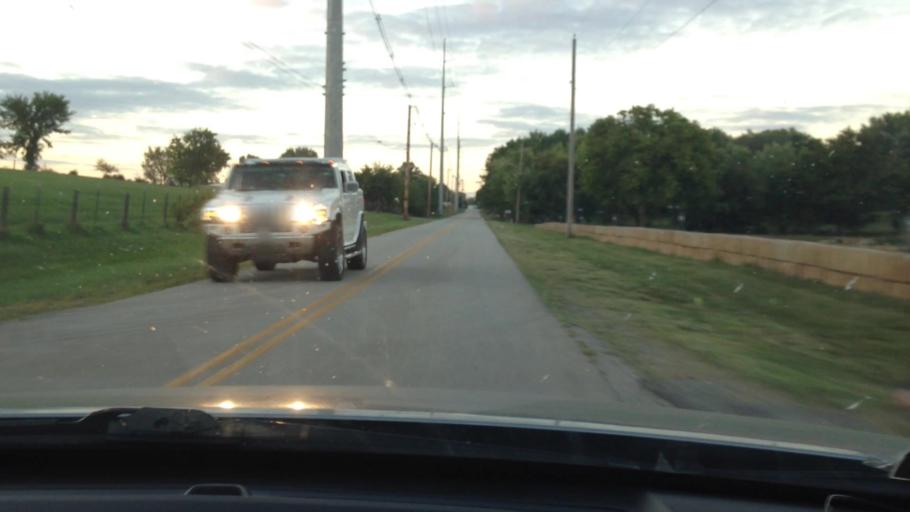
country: US
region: Kansas
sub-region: Leavenworth County
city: Lansing
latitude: 39.1821
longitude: -94.8453
